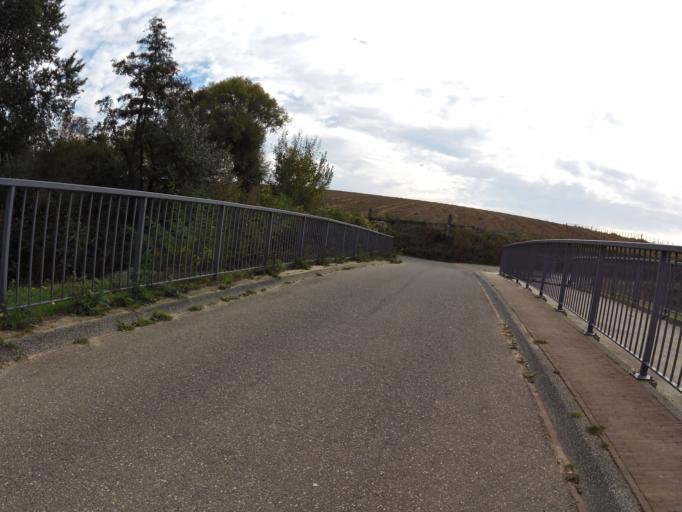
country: NL
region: Limburg
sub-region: Gemeente Voerendaal
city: Ubachsberg
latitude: 50.8221
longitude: 5.9376
